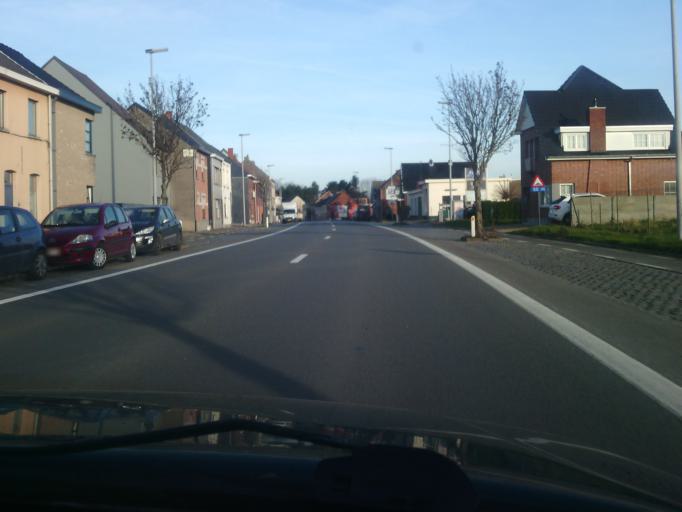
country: BE
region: Flanders
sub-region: Provincie Oost-Vlaanderen
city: Dendermonde
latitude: 51.0272
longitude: 4.0614
